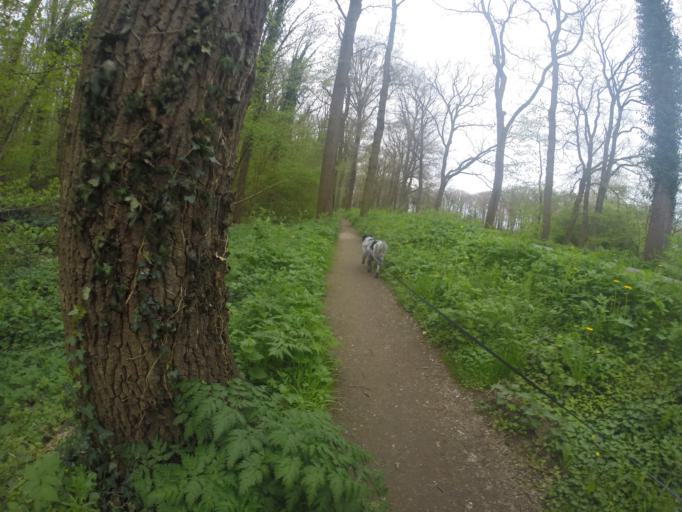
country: NL
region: Gelderland
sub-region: Gemeente Zutphen
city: Leesten
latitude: 52.1033
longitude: 6.2705
